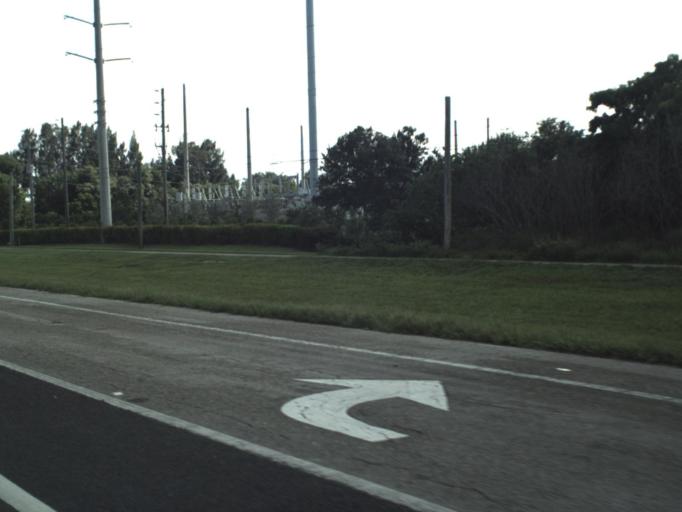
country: US
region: Florida
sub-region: Palm Beach County
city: Villages of Oriole
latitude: 26.4294
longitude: -80.2044
